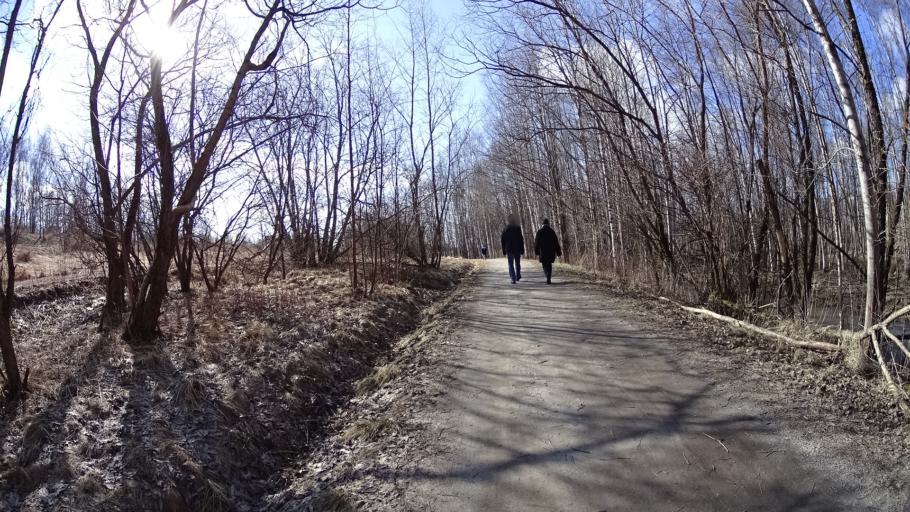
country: FI
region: Uusimaa
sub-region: Helsinki
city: Teekkarikylae
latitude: 60.2122
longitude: 24.8424
